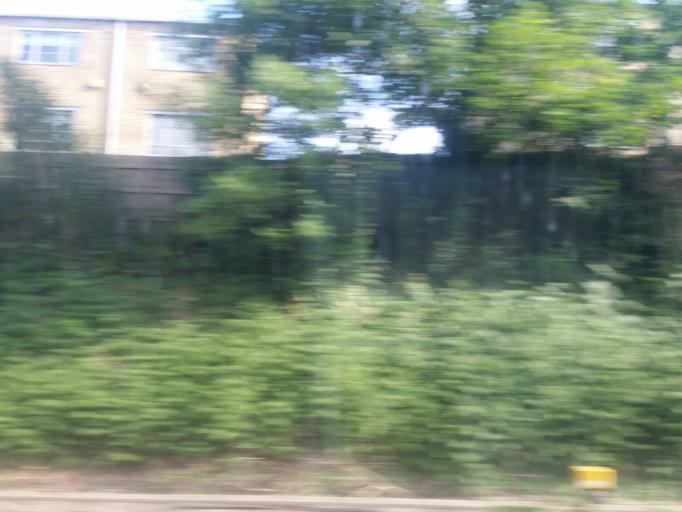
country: GB
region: England
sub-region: Greater London
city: Islington
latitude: 51.5489
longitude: -0.0895
